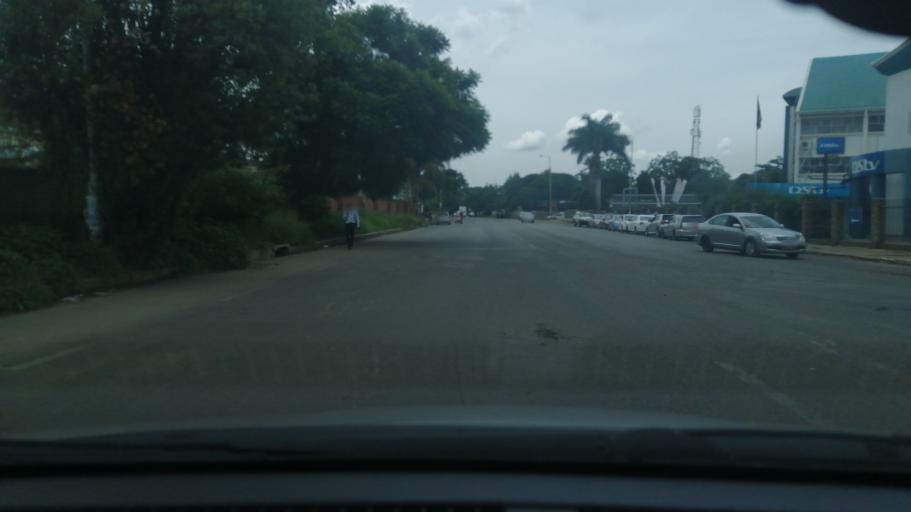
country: ZW
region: Harare
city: Harare
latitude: -17.8042
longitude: 31.0380
